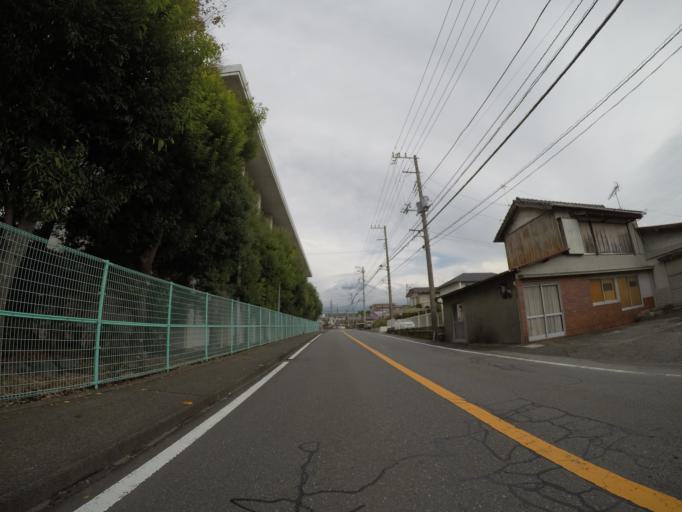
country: JP
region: Shizuoka
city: Fuji
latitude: 35.1952
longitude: 138.6535
